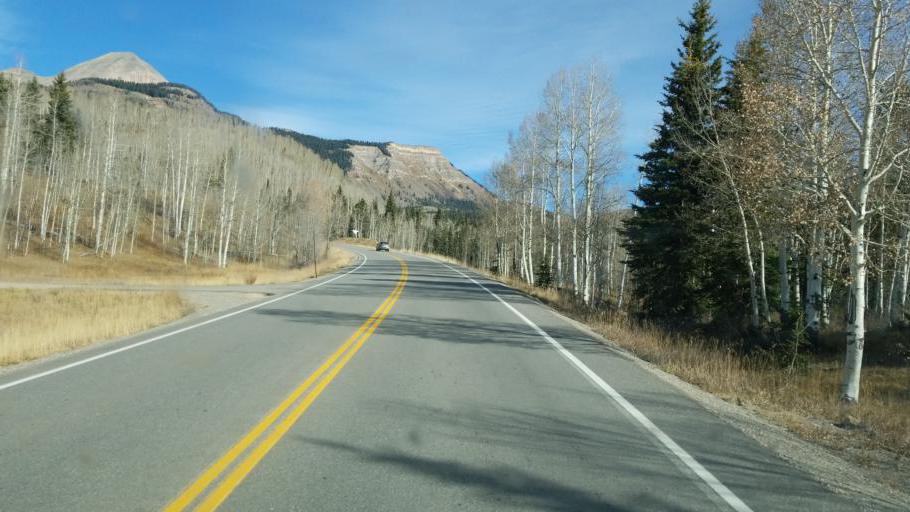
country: US
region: Colorado
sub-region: San Juan County
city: Silverton
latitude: 37.6602
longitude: -107.7981
